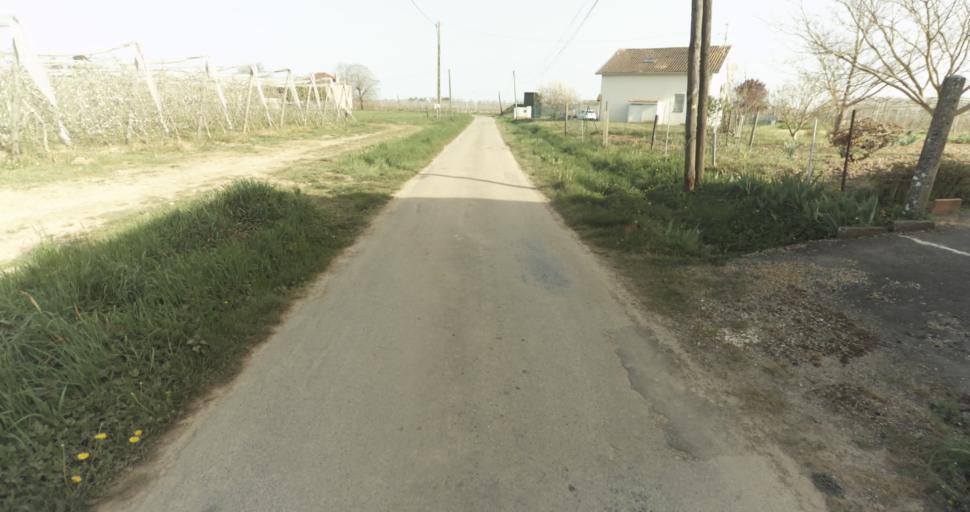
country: FR
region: Midi-Pyrenees
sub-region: Departement du Tarn-et-Garonne
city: Moissac
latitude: 44.1030
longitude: 1.1360
